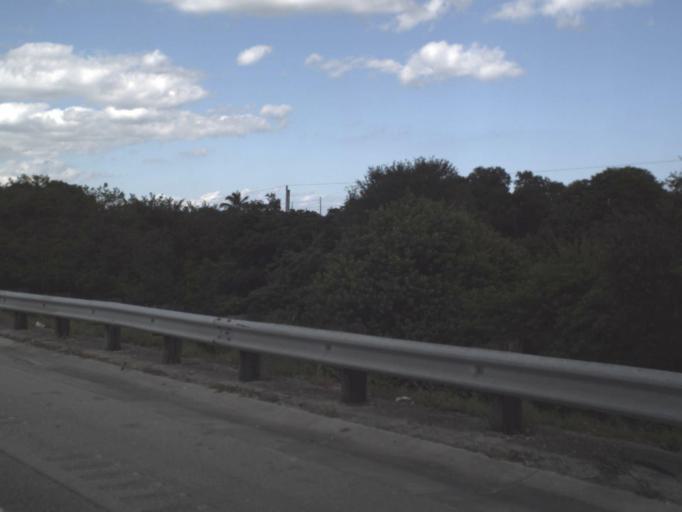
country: US
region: Florida
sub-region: Broward County
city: Pembroke Pines
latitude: 26.0253
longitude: -80.2130
